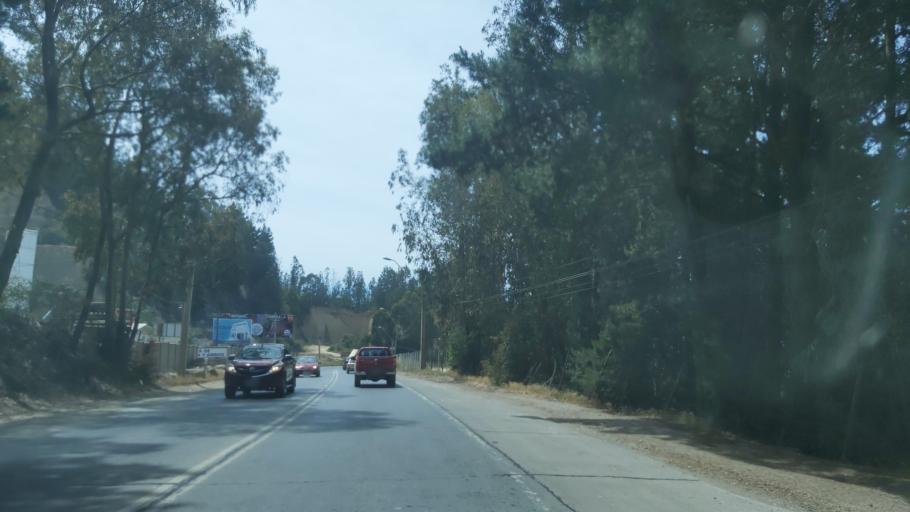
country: CL
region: Maule
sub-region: Provincia de Talca
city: Constitucion
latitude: -35.3493
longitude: -72.4132
